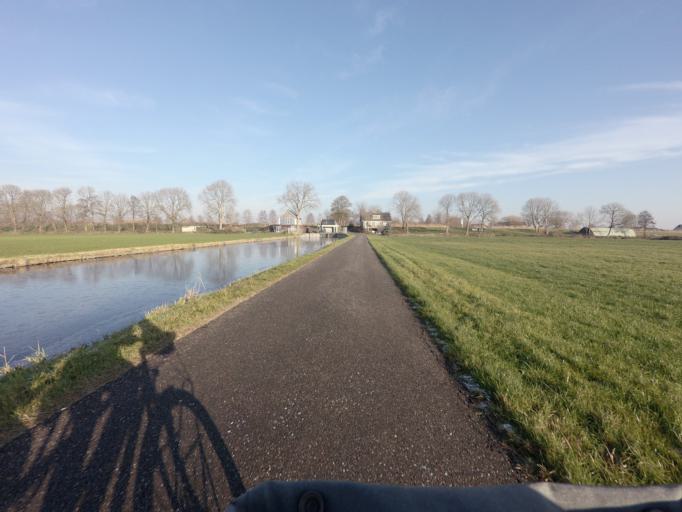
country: NL
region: Utrecht
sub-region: Gemeente De Ronde Venen
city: Mijdrecht
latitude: 52.1752
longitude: 4.8598
